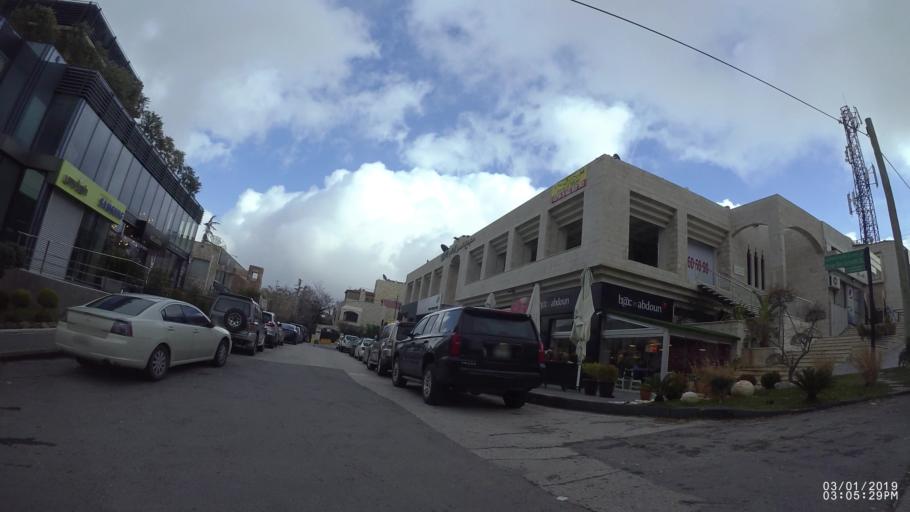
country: JO
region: Amman
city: Amman
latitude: 31.9536
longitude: 35.8839
